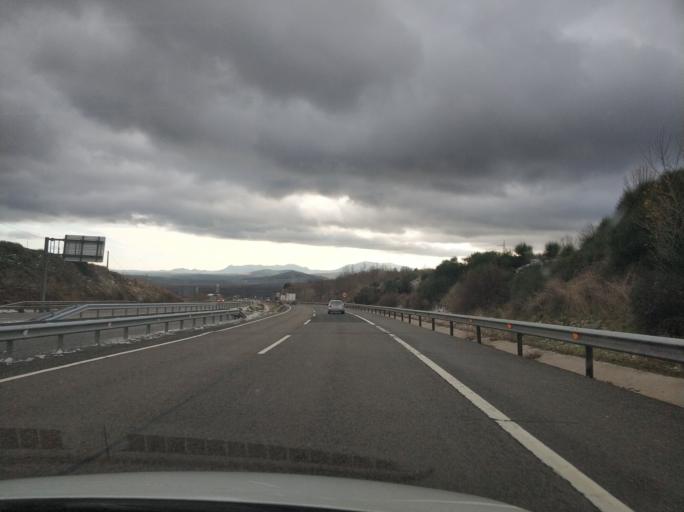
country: ES
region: Madrid
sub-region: Provincia de Madrid
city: Robregordo
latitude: 41.0941
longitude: -3.5949
